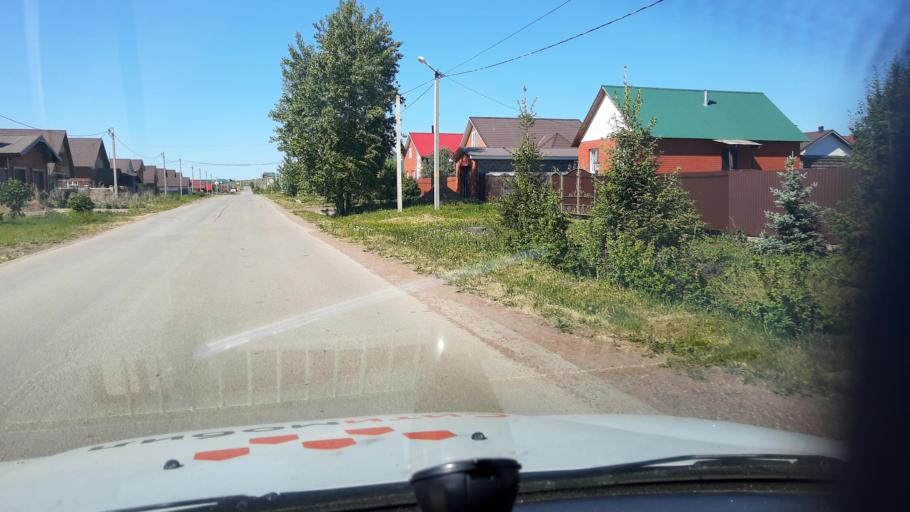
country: RU
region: Bashkortostan
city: Kabakovo
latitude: 54.6597
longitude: 56.2140
